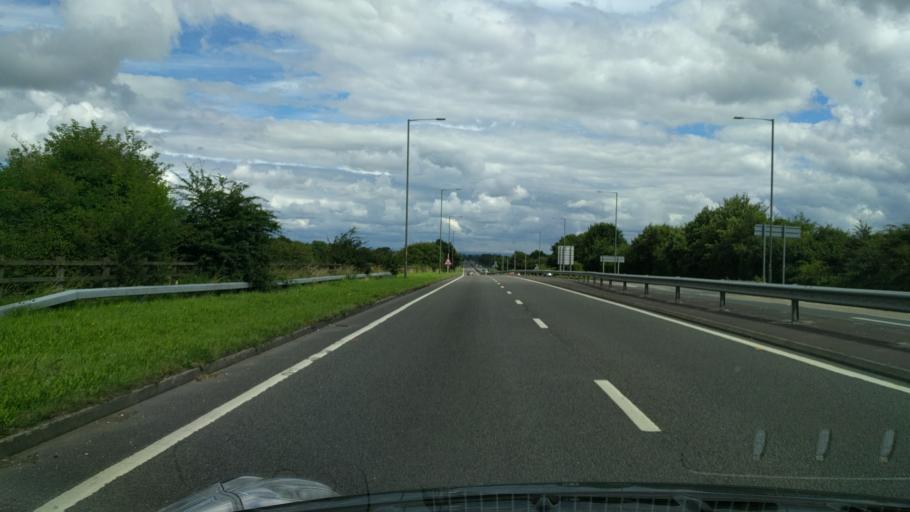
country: GB
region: England
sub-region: Borough of Wigan
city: Leigh
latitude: 53.4721
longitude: -2.5353
